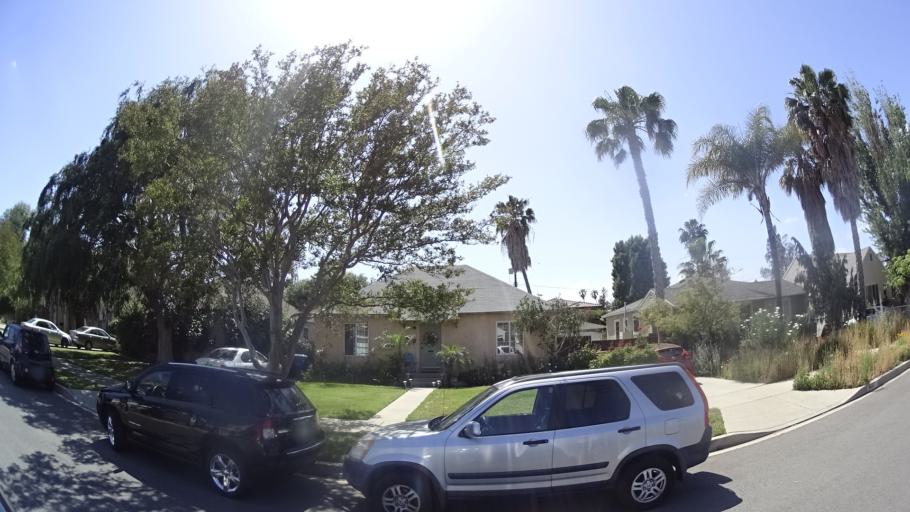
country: US
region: California
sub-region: Los Angeles County
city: Sherman Oaks
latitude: 34.1537
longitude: -118.4433
